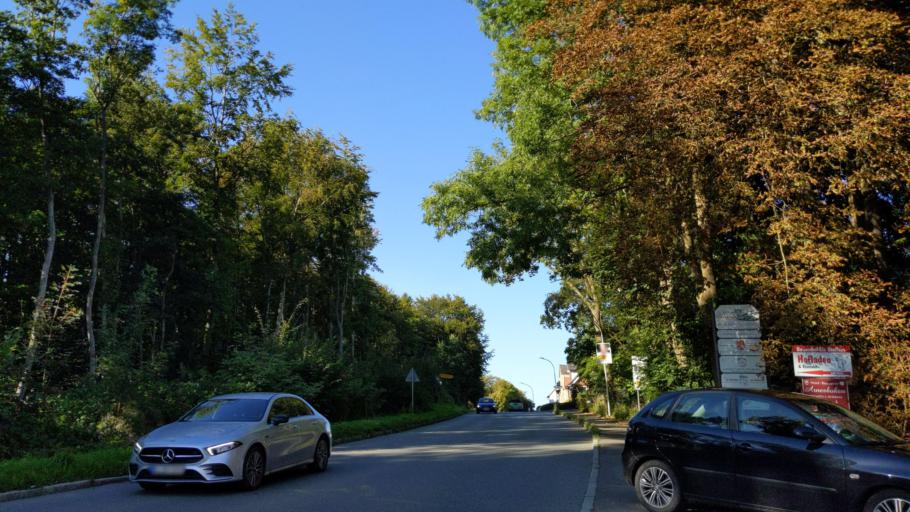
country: DE
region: Schleswig-Holstein
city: Ahrensbok
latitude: 53.9994
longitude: 10.5779
